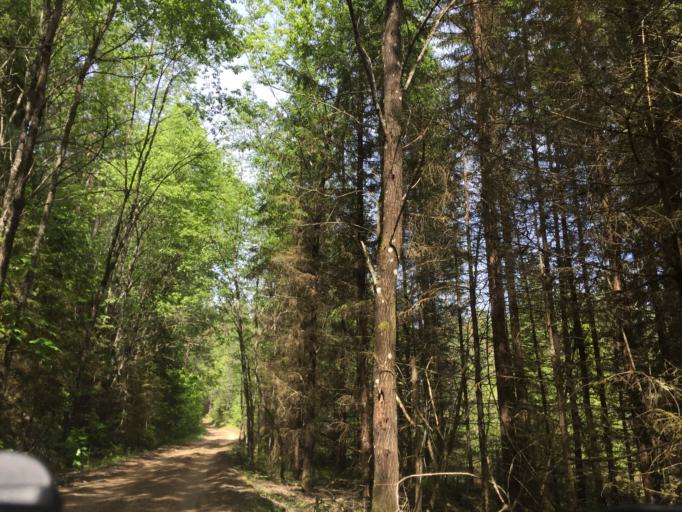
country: LV
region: Koceni
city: Koceni
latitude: 57.4407
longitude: 25.2838
